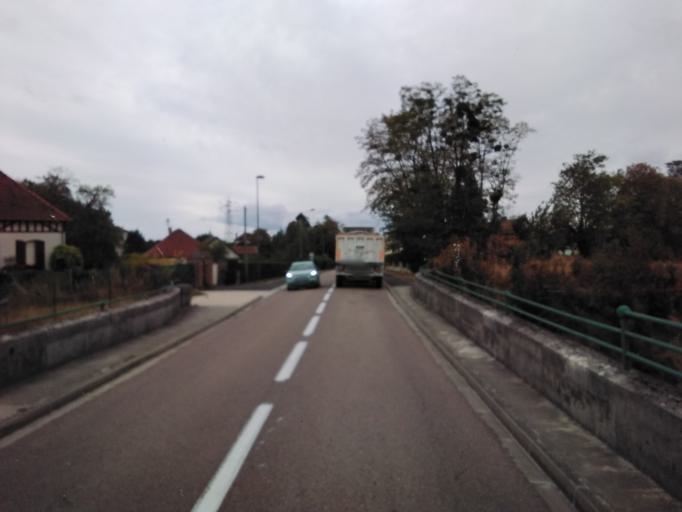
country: FR
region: Champagne-Ardenne
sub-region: Departement de l'Aube
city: Vendeuvre-sur-Barse
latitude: 48.2413
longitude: 4.4759
